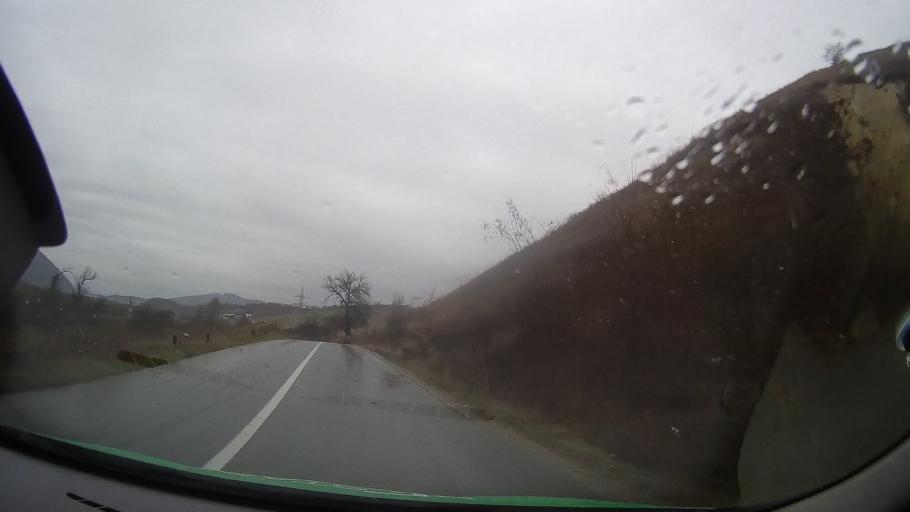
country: RO
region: Bistrita-Nasaud
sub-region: Comuna Mariselu
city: Mariselu
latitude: 47.0447
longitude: 24.4661
